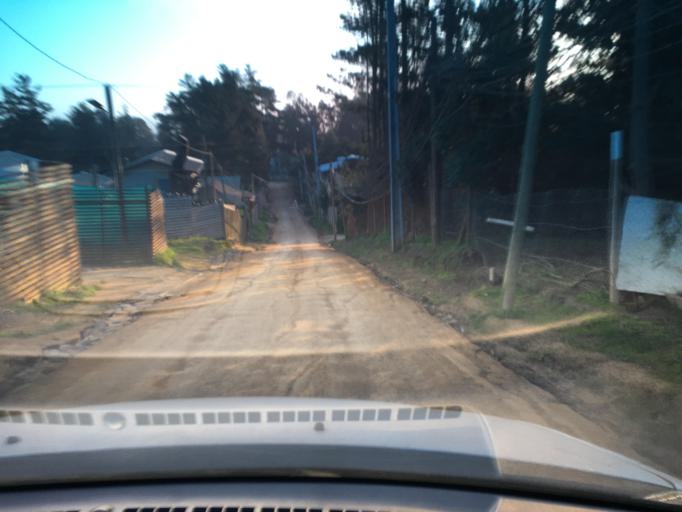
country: CL
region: Valparaiso
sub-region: San Antonio Province
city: El Tabo
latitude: -33.4507
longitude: -71.6488
